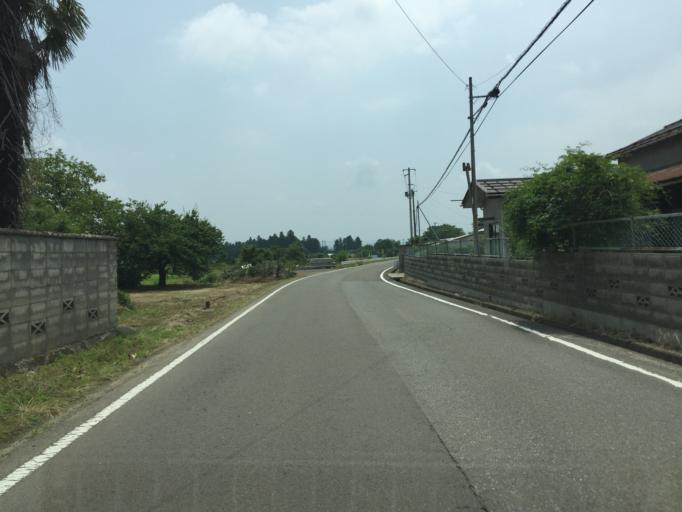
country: JP
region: Fukushima
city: Fukushima-shi
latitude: 37.7641
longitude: 140.3729
